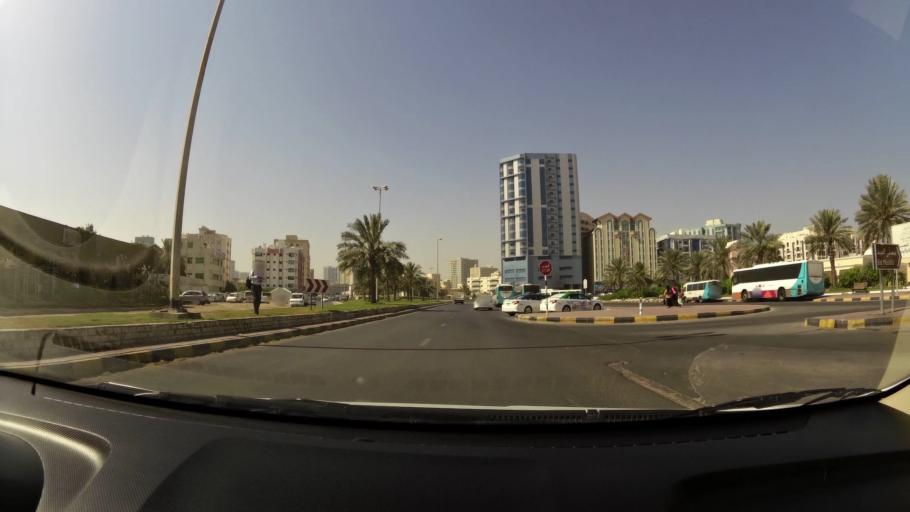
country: AE
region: Ajman
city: Ajman
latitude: 25.4114
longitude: 55.4463
